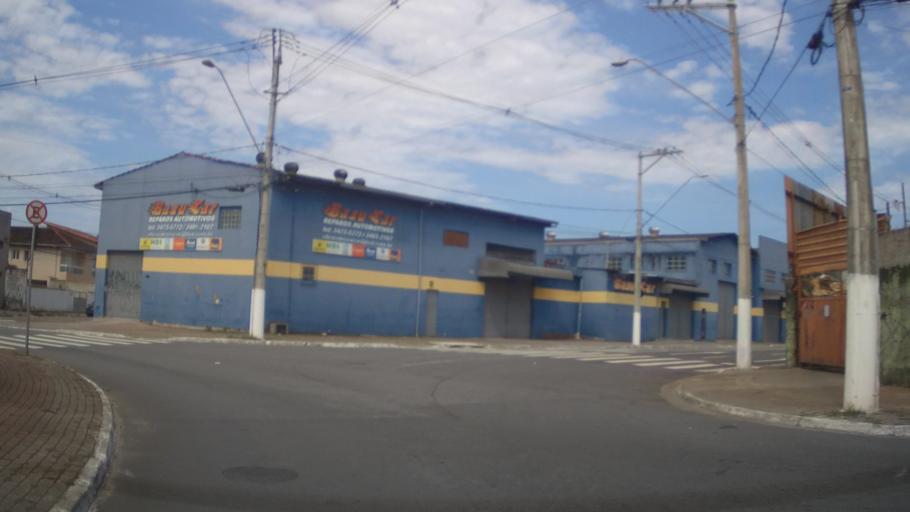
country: BR
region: Sao Paulo
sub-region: Praia Grande
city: Praia Grande
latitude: -24.0020
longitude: -46.4253
